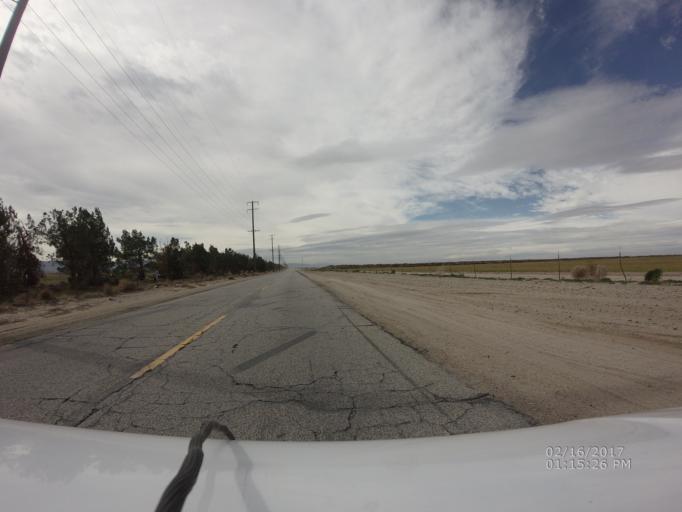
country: US
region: California
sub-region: Los Angeles County
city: Palmdale
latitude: 34.6313
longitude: -118.0210
